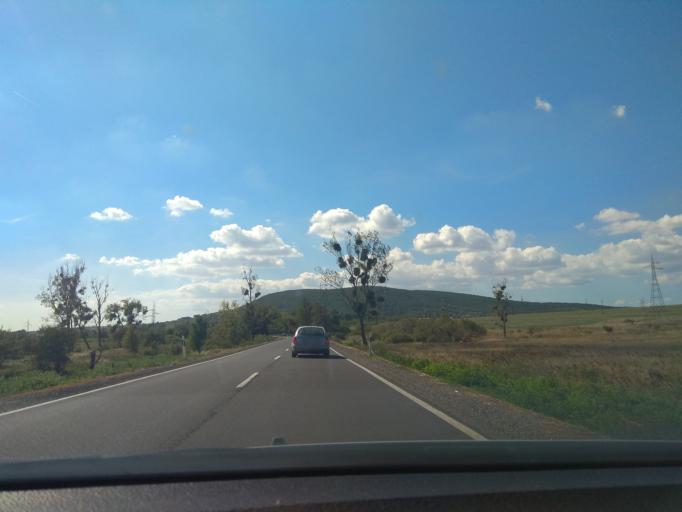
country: HU
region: Borsod-Abauj-Zemplen
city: Sarospatak
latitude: 48.3683
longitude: 21.6001
